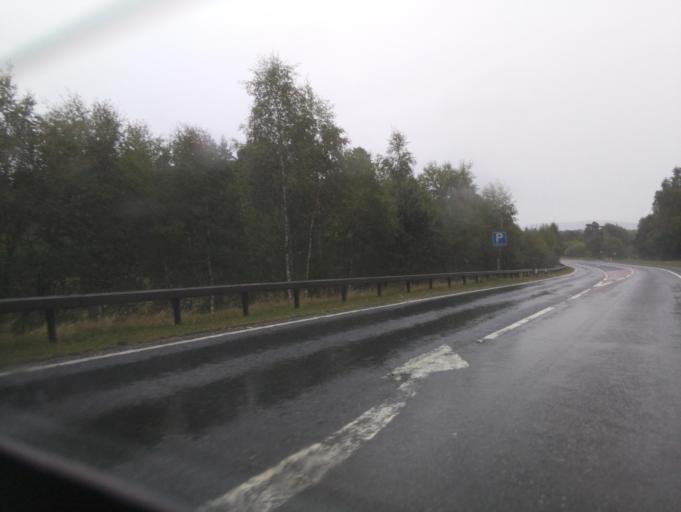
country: GB
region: Scotland
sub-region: Highland
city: Grantown on Spey
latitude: 57.3202
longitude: -3.6169
